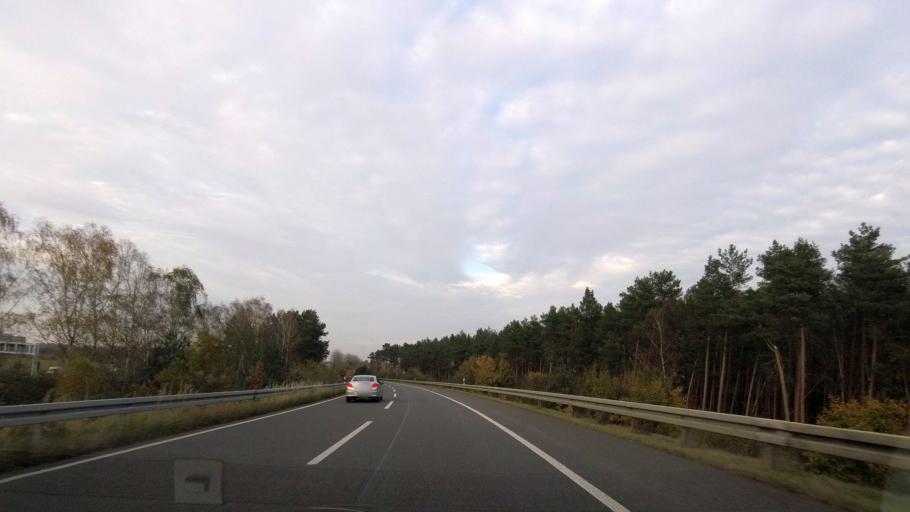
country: DE
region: Brandenburg
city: Schulzendorf
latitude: 52.3225
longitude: 13.5554
